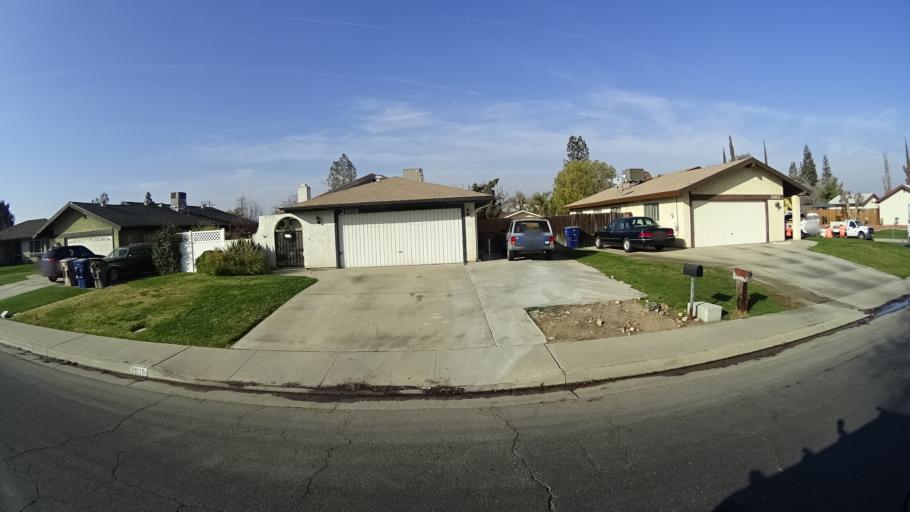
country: US
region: California
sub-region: Kern County
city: Oildale
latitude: 35.4003
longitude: -118.9289
